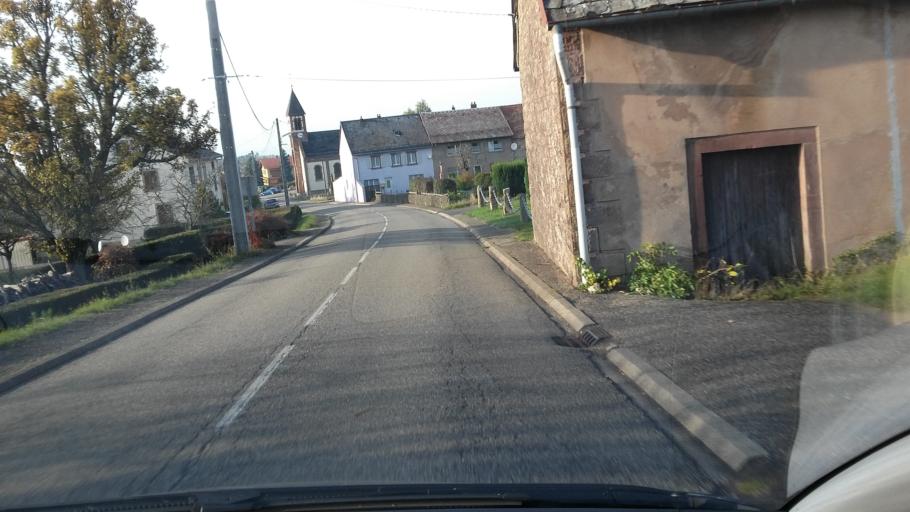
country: FR
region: Lorraine
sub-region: Departement de la Moselle
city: Dabo
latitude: 48.6808
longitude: 7.2298
